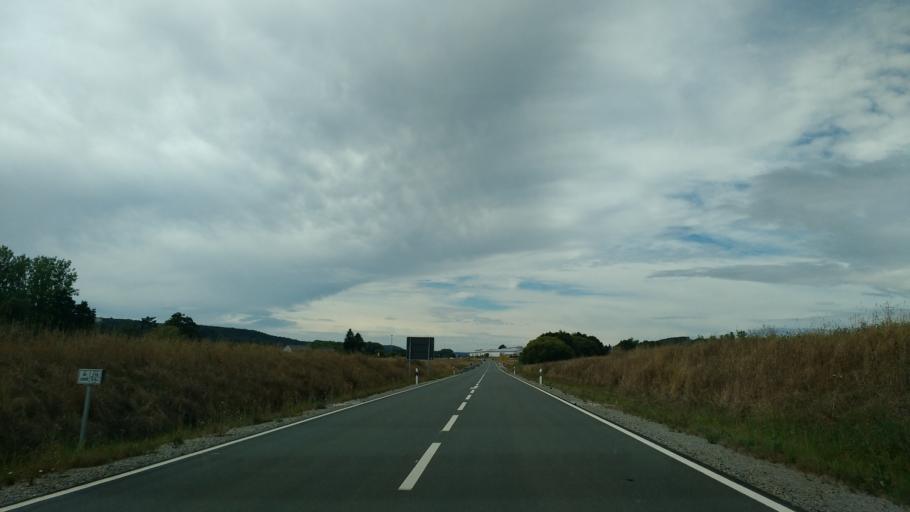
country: DE
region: Bavaria
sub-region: Regierungsbezirk Mittelfranken
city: Burghaslach
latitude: 49.7655
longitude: 10.5754
